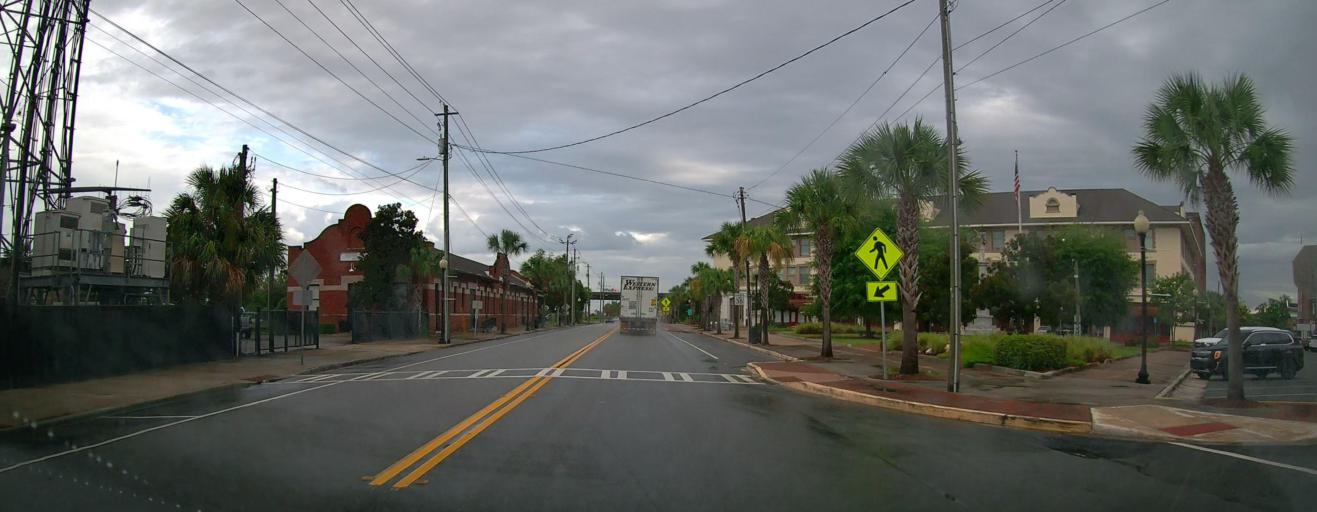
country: US
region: Georgia
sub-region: Ware County
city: Waycross
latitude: 31.2097
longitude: -82.3590
